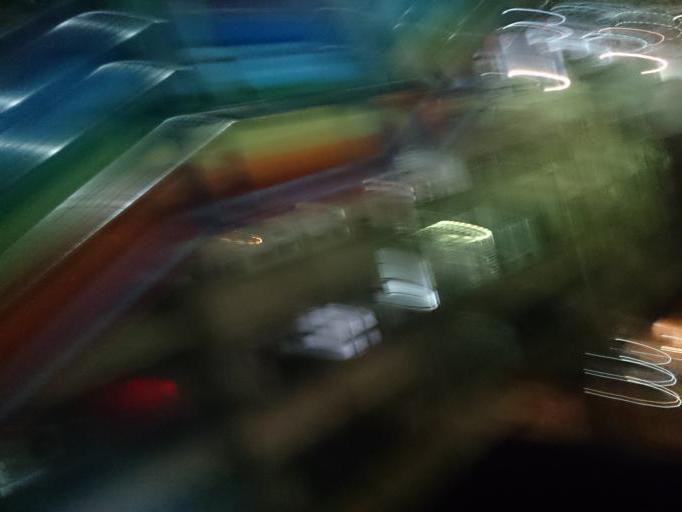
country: TW
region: Taipei
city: Taipei
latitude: 25.0515
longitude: 121.5770
